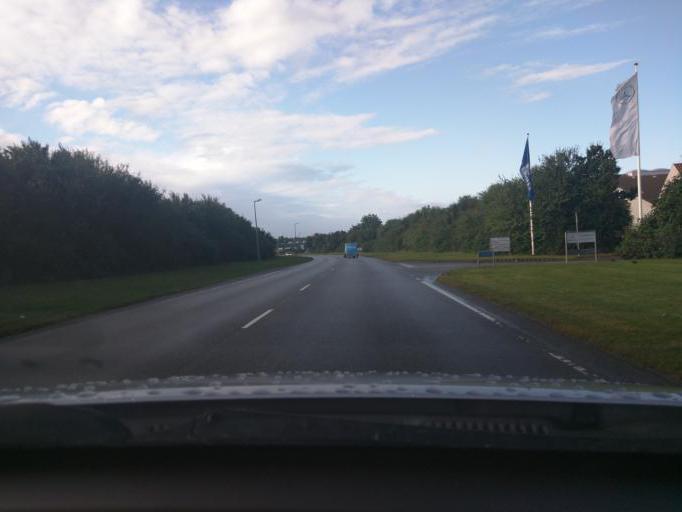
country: DK
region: Central Jutland
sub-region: Viborg Kommune
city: Viborg
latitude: 56.4621
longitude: 9.3759
